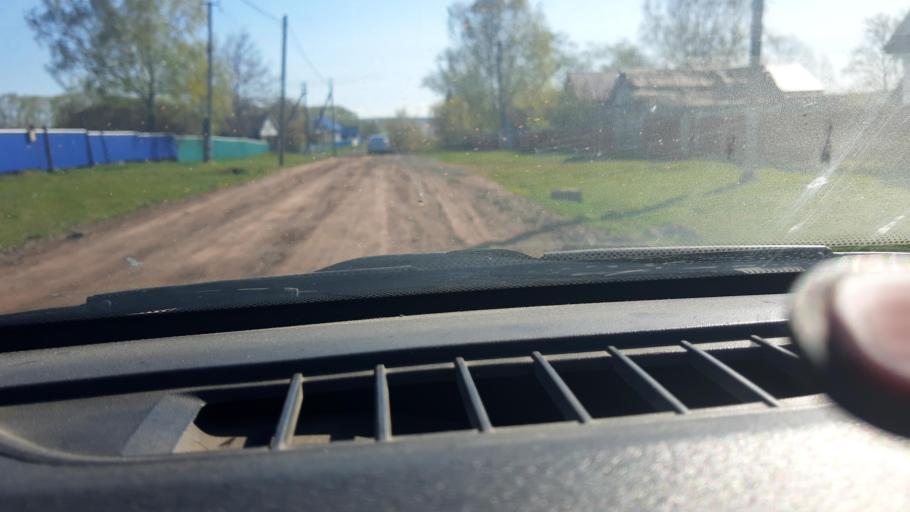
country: RU
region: Bashkortostan
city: Chishmy
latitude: 54.5942
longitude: 55.2686
